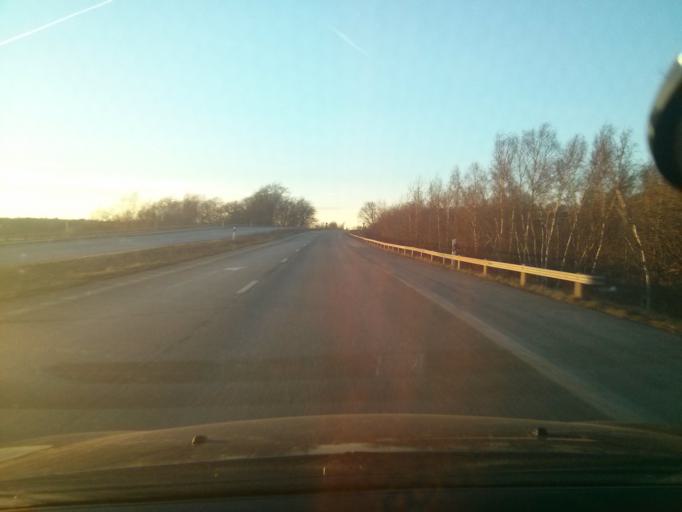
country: SE
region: Blekinge
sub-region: Karlskrona Kommun
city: Rodeby
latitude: 56.2110
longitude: 15.5981
